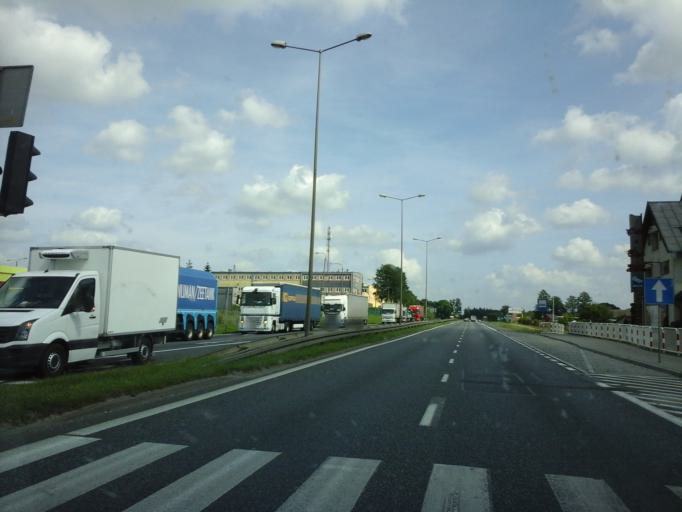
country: PL
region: Lodz Voivodeship
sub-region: Powiat lodzki wschodni
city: Tuszyn
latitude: 51.5999
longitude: 19.5430
